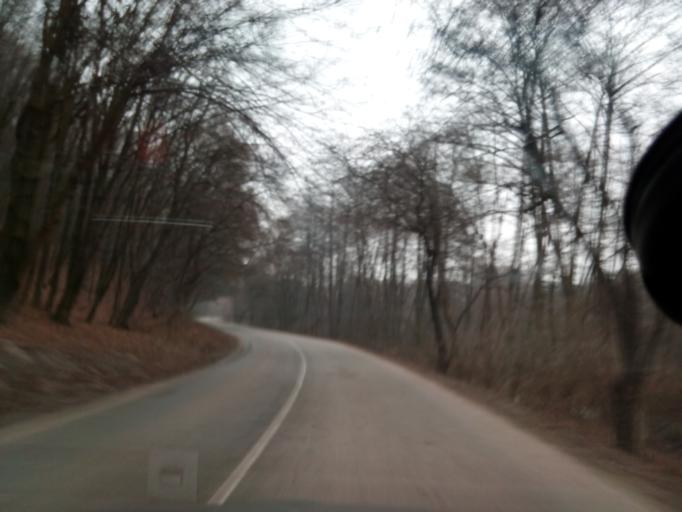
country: SK
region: Kosicky
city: Medzev
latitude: 48.6931
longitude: 20.9488
